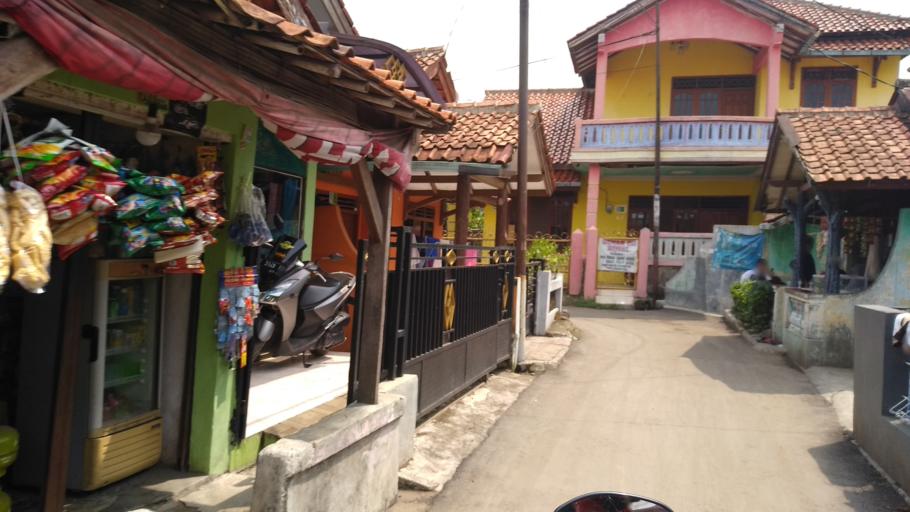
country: ID
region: West Java
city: Ciampea
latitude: -6.5597
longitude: 106.7462
